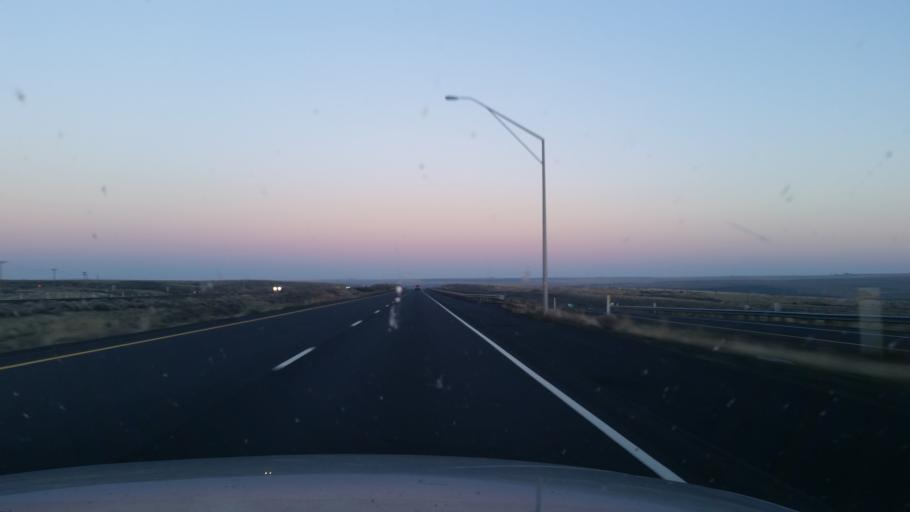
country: US
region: Washington
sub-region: Adams County
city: Ritzville
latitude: 47.0970
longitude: -118.6733
